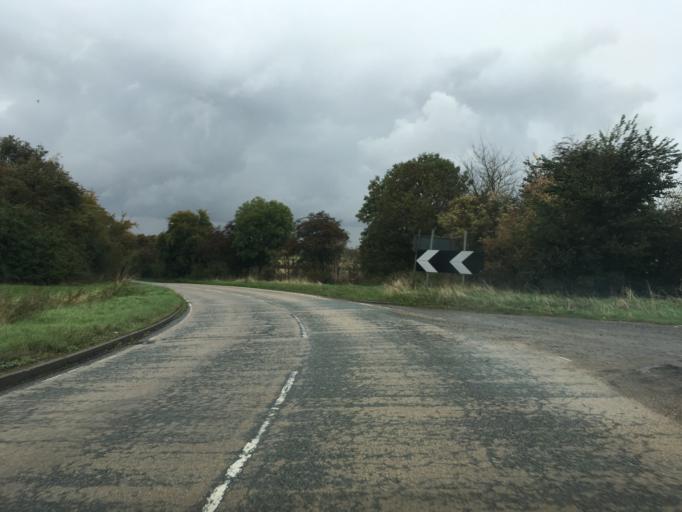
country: GB
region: England
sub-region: Nottinghamshire
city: Ruddington
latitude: 52.8934
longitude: -1.1206
